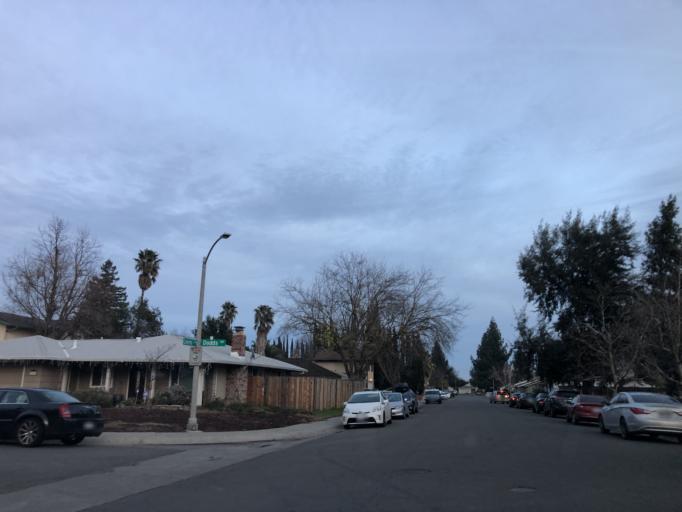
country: US
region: California
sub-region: Yolo County
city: Woodland
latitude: 38.6714
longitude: -121.7596
